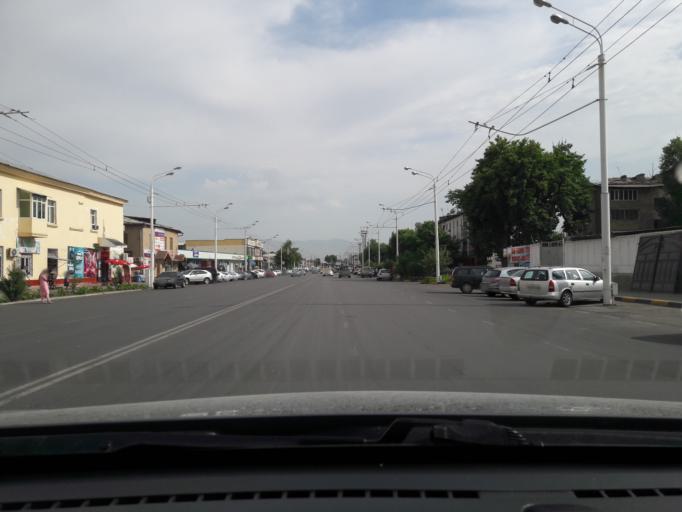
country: TJ
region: Dushanbe
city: Dushanbe
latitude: 38.5455
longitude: 68.7553
